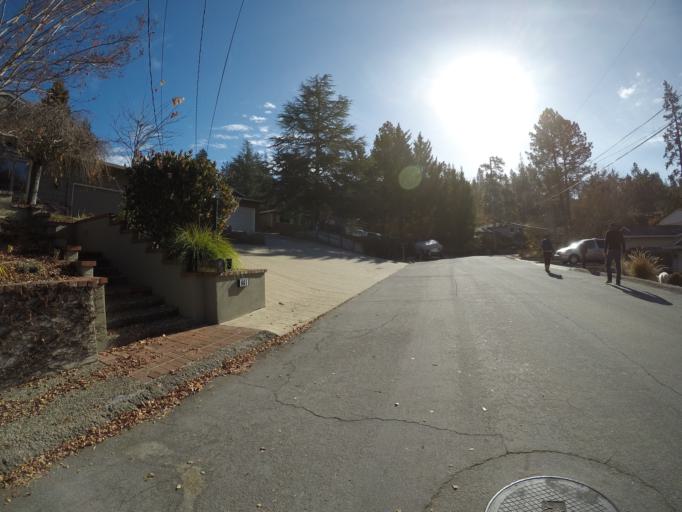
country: US
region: California
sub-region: Santa Cruz County
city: Mount Hermon
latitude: 37.0401
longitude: -122.0369
